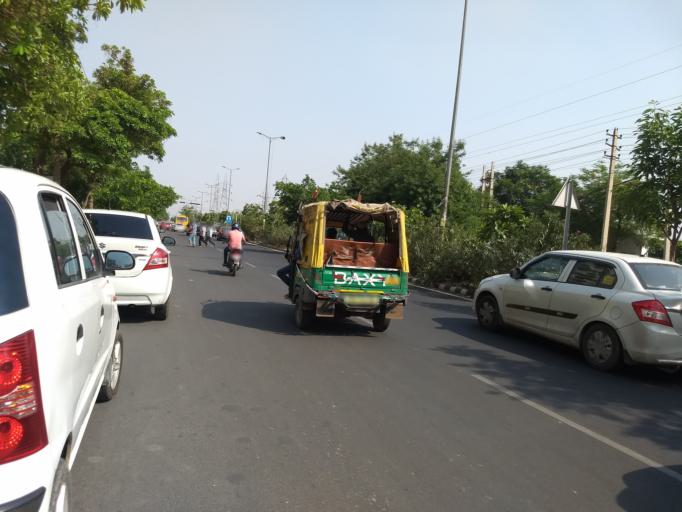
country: IN
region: Haryana
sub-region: Gurgaon
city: Gurgaon
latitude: 28.4404
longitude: 77.0417
